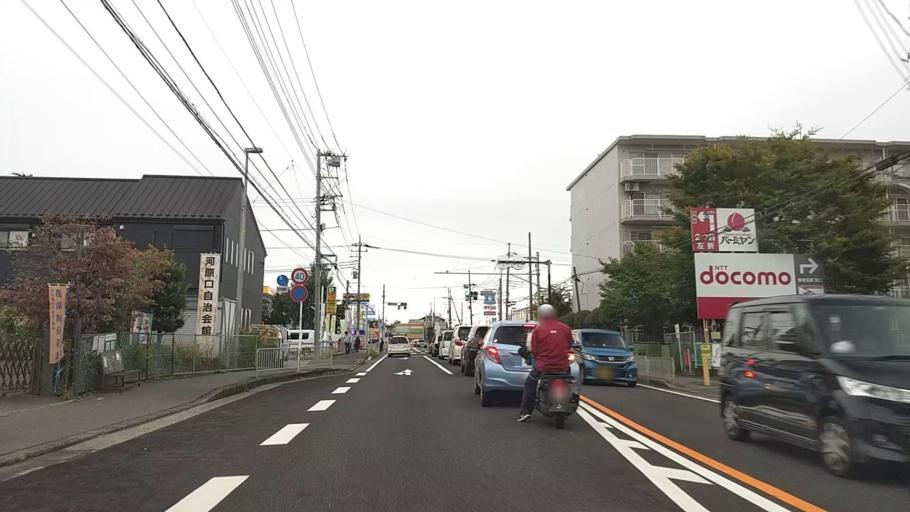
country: JP
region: Kanagawa
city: Atsugi
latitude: 35.4482
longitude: 139.3778
